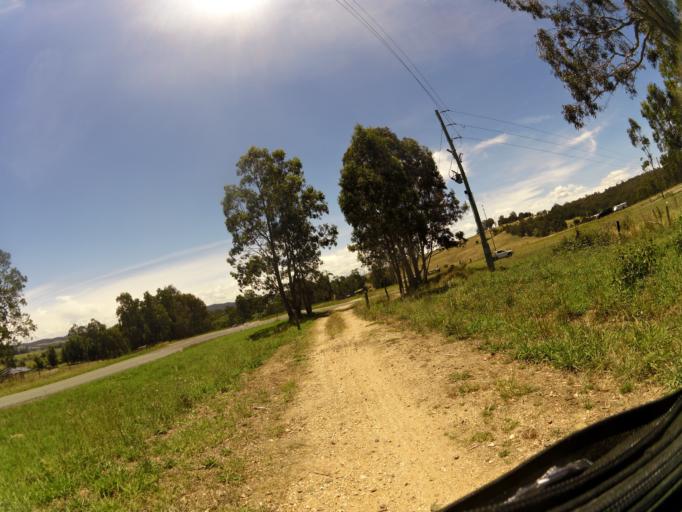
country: AU
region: Victoria
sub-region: East Gippsland
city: Lakes Entrance
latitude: -37.7221
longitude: 147.8480
